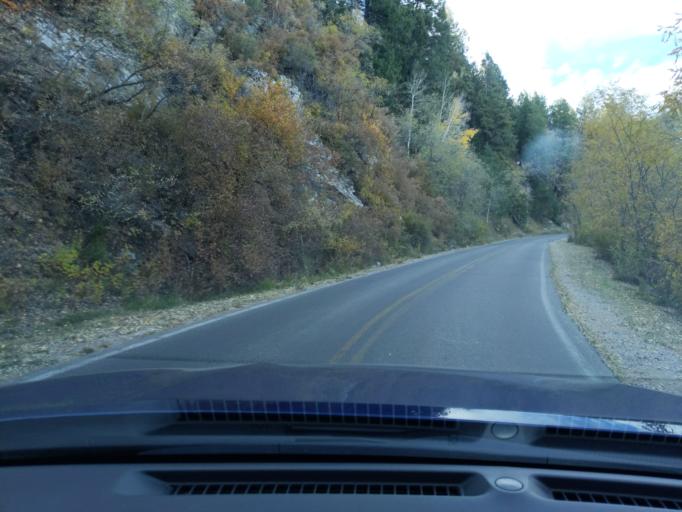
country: US
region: Arizona
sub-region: Pima County
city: Catalina
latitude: 32.4489
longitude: -110.7824
